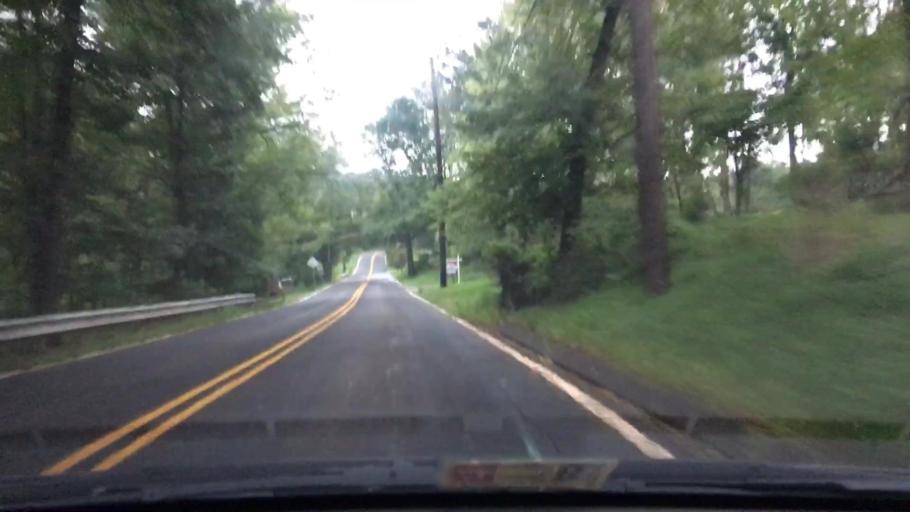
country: US
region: Maryland
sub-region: Montgomery County
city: Montgomery Village
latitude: 39.2040
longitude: -77.1625
